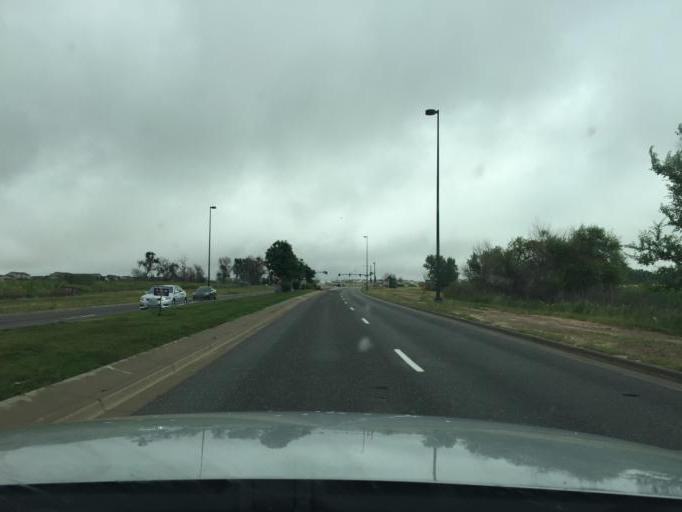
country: US
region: Colorado
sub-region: Adams County
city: Aurora
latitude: 39.7984
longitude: -104.7754
